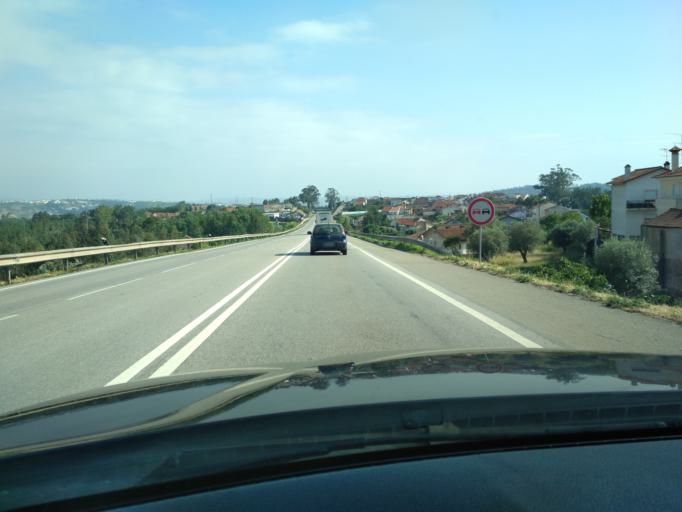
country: PT
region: Aveiro
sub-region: Mealhada
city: Pampilhosa do Botao
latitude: 40.2967
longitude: -8.4462
